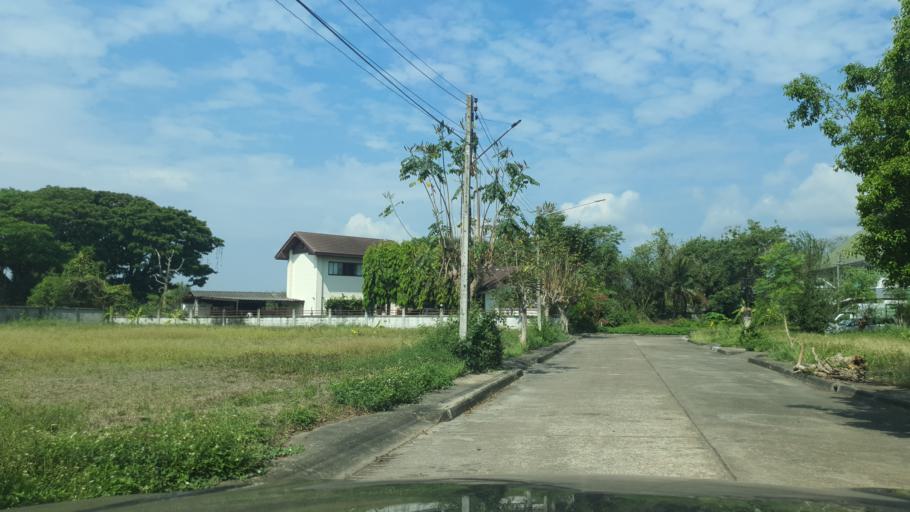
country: TH
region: Chiang Mai
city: Hang Dong
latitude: 18.7271
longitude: 98.9437
